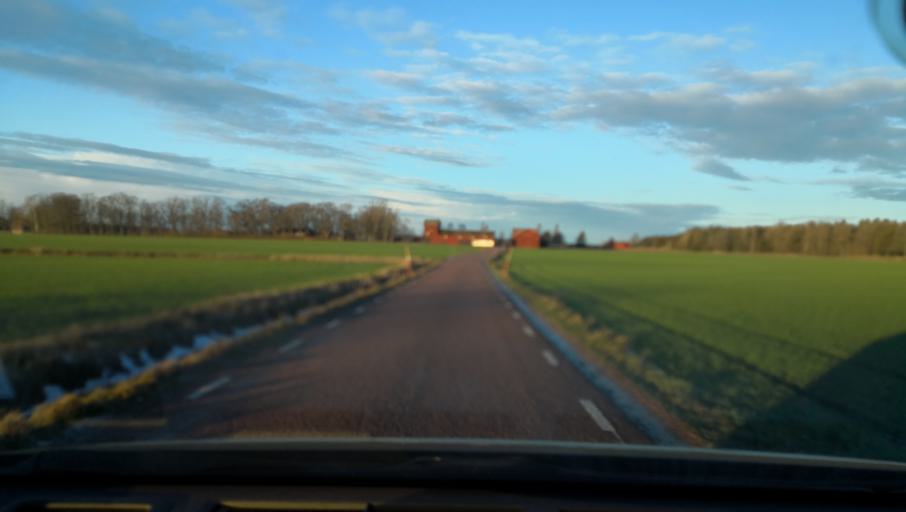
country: SE
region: Vaestmanland
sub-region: Vasteras
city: Tillberga
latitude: 59.6955
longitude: 16.5998
